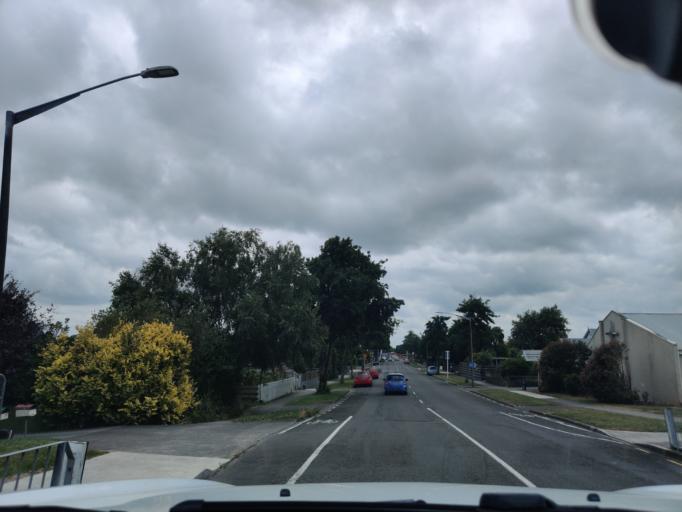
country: NZ
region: Manawatu-Wanganui
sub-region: Palmerston North City
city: Palmerston North
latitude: -40.3533
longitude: 175.5866
